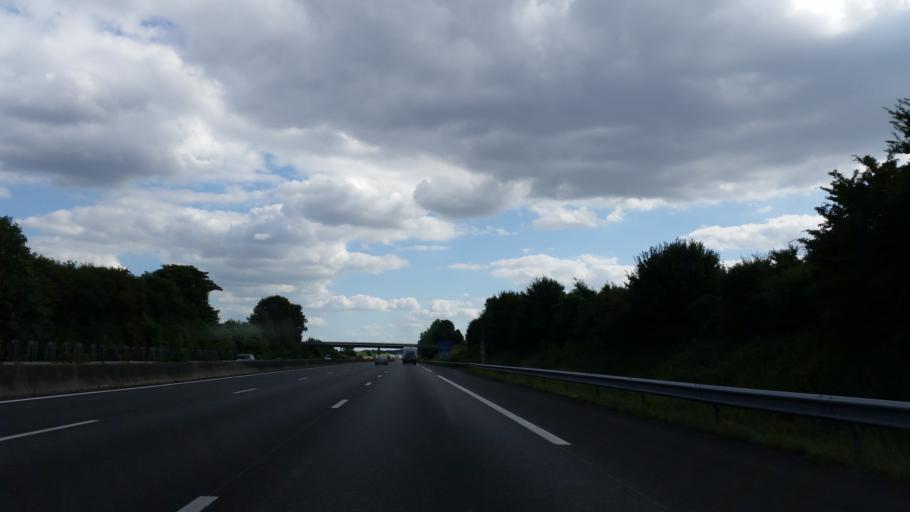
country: FR
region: Nord-Pas-de-Calais
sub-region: Departement du Pas-de-Calais
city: Bapaume
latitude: 50.0744
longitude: 2.8707
